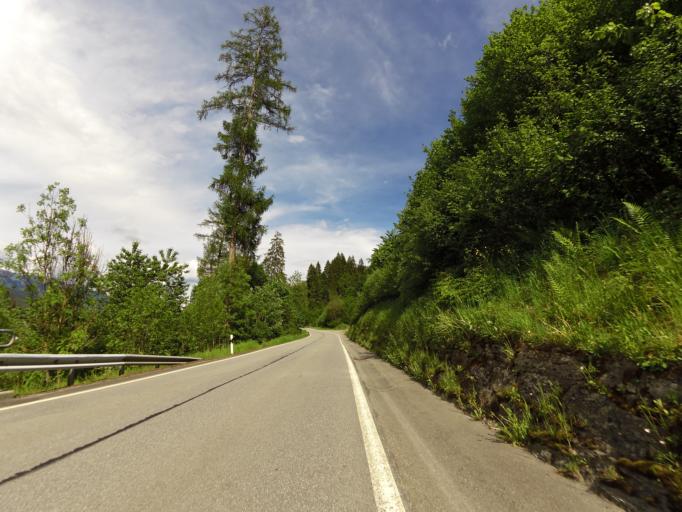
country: CH
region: Grisons
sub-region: Surselva District
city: Laax
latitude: 46.7805
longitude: 9.2537
